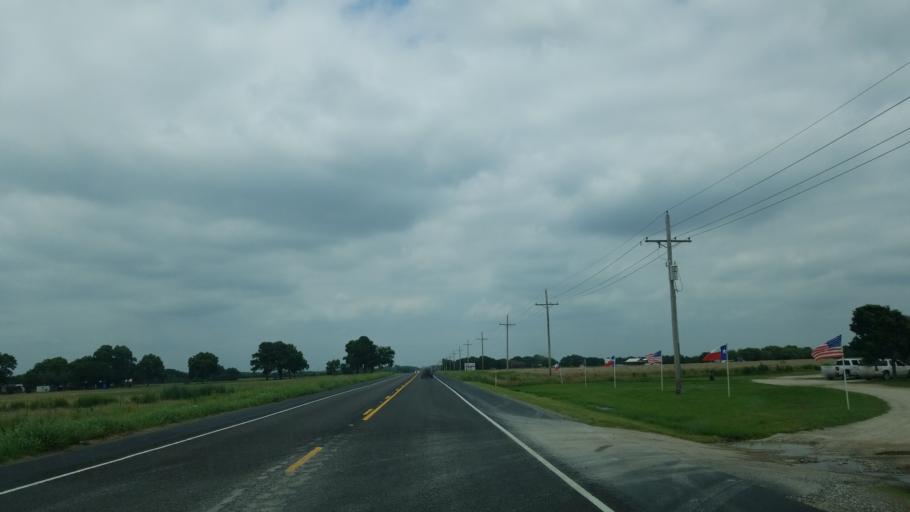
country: US
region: Texas
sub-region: Denton County
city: Pilot Point
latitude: 33.4224
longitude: -96.9362
